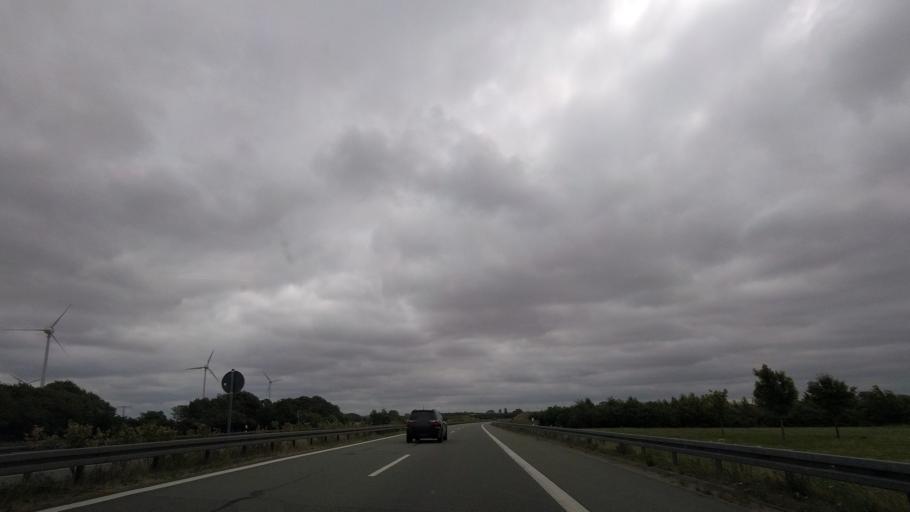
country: DE
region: Mecklenburg-Vorpommern
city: Brandshagen
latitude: 54.2414
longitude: 13.1428
